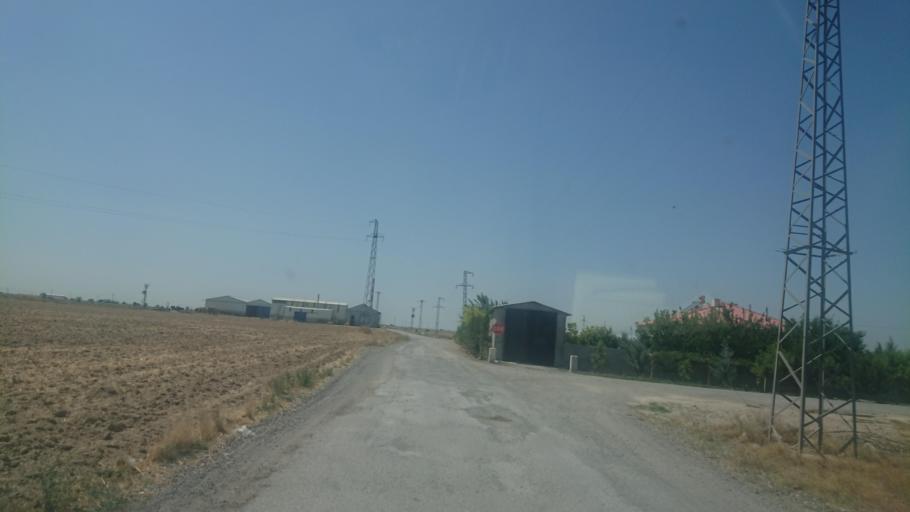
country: TR
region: Aksaray
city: Sultanhani
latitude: 38.2852
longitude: 33.7115
